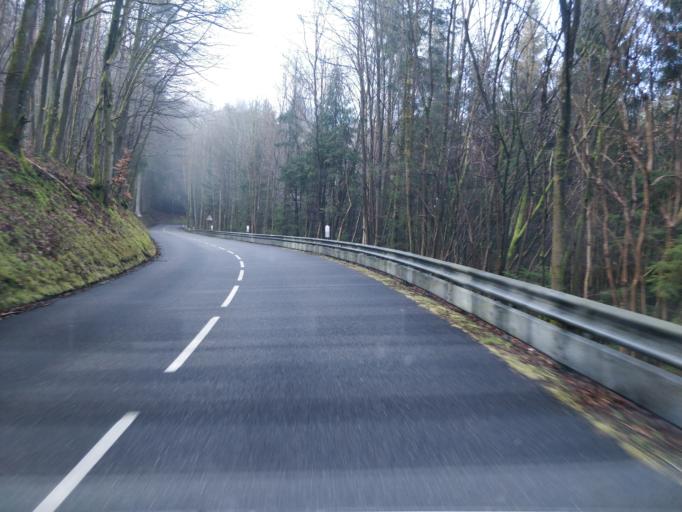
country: FR
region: Lorraine
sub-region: Departement de la Moselle
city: Soucht
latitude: 48.9180
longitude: 7.3274
